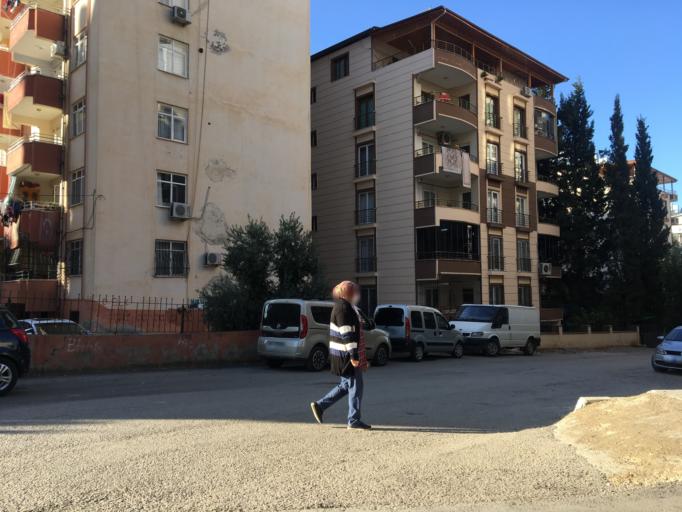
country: TR
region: Hatay
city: Kirikhan
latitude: 36.4930
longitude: 36.3414
